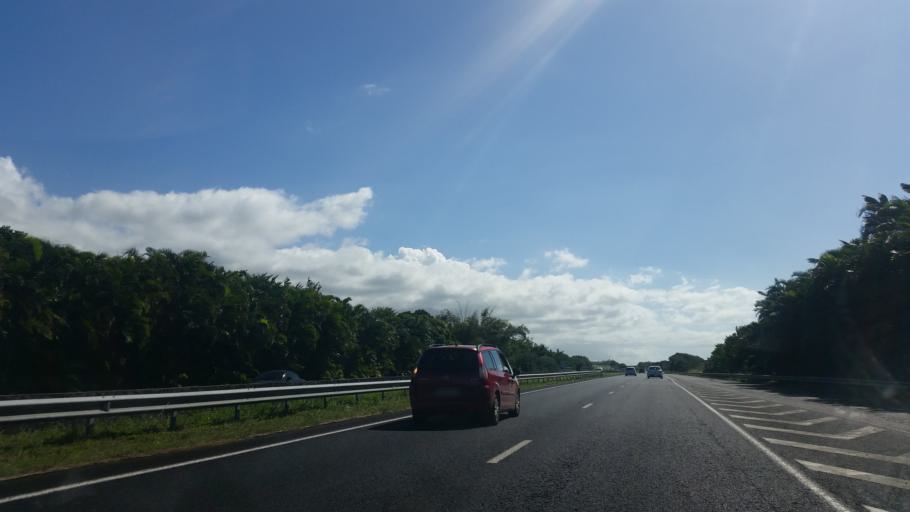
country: RE
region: Reunion
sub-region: Reunion
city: Bras-Panon
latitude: -21.0006
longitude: 55.6751
